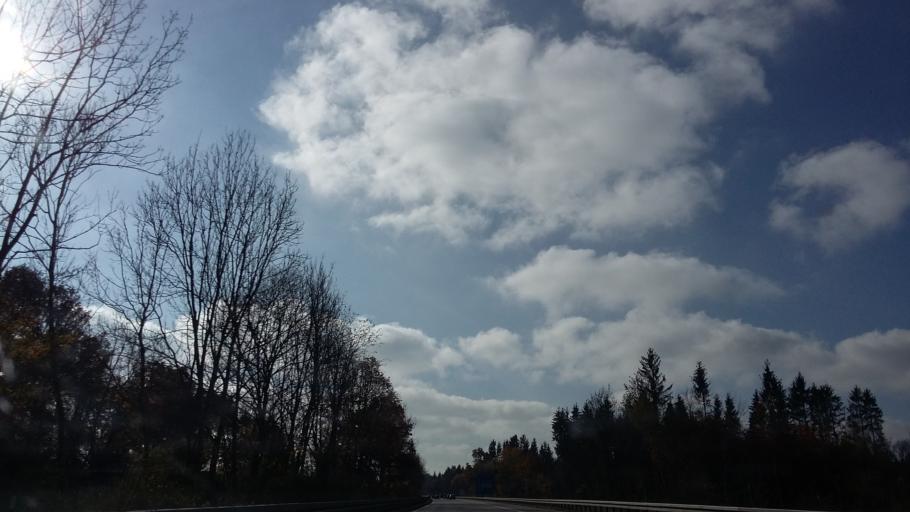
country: DE
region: Bavaria
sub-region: Upper Bavaria
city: Unterhaching
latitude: 48.0667
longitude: 11.5964
